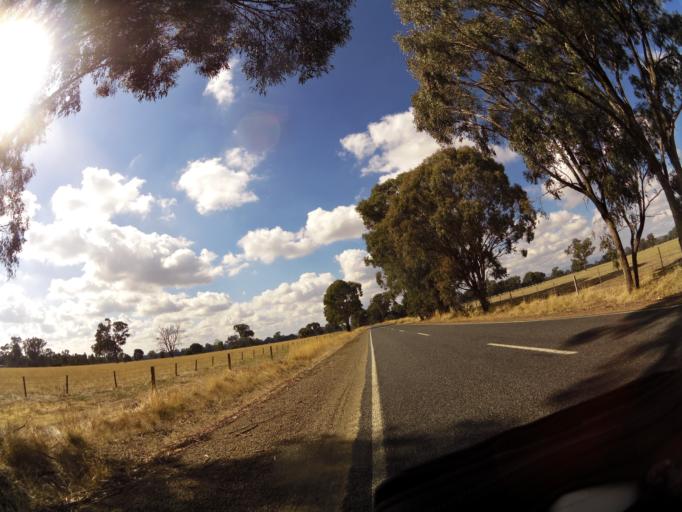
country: AU
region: Victoria
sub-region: Benalla
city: Benalla
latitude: -36.6077
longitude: 146.0160
